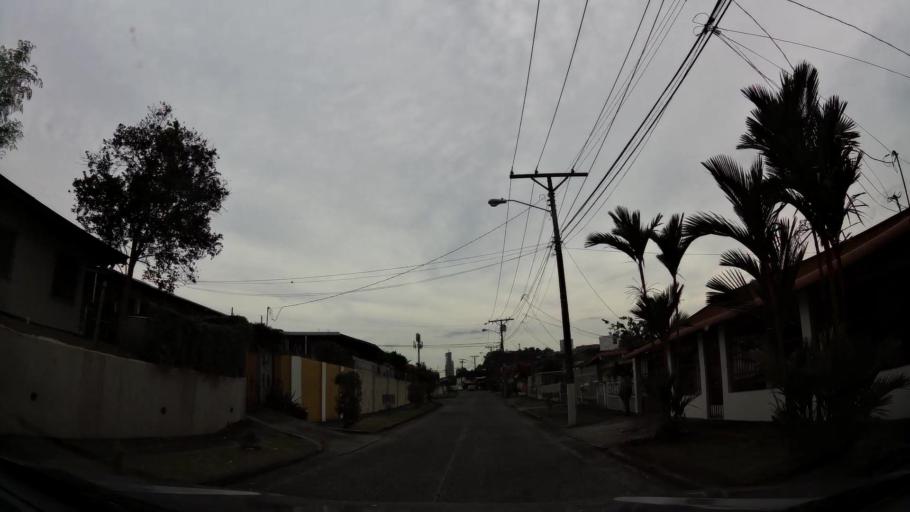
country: PA
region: Panama
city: Panama
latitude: 9.0207
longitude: -79.5257
